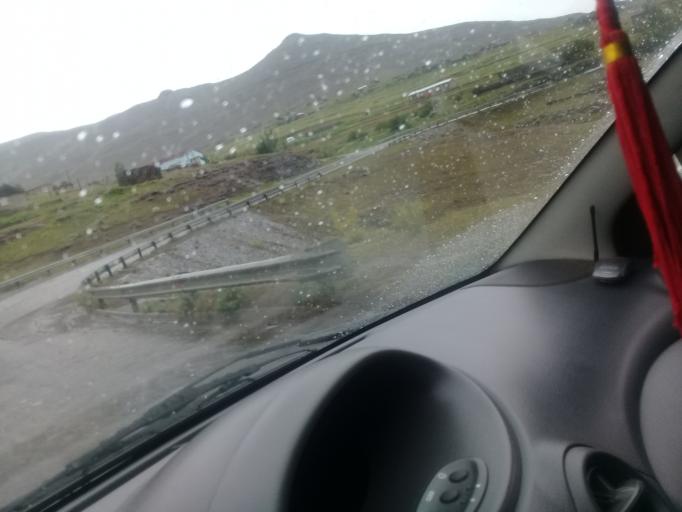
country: LS
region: Mokhotlong
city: Mokhotlong
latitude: -29.3011
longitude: 29.0393
